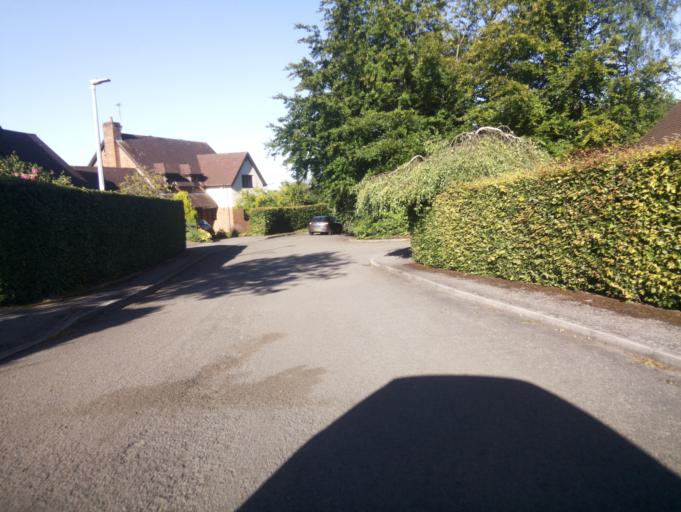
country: GB
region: Wales
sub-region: Monmouthshire
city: Tintern
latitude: 51.6879
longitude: -2.7500
